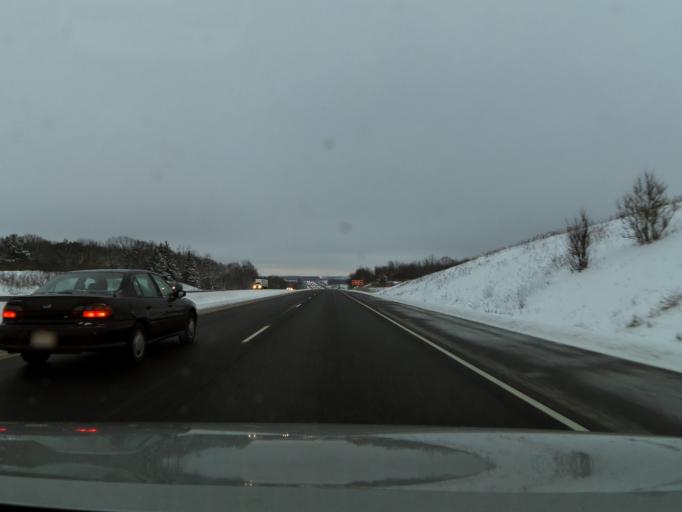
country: US
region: Wisconsin
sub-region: Saint Croix County
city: Woodville
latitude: 44.9349
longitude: -92.2949
